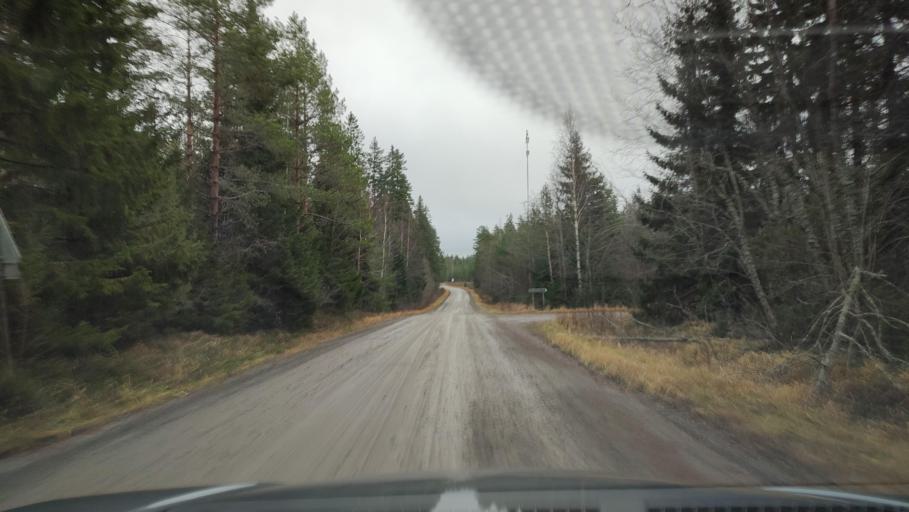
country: FI
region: Southern Ostrobothnia
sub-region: Suupohja
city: Karijoki
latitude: 62.1375
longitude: 21.6602
